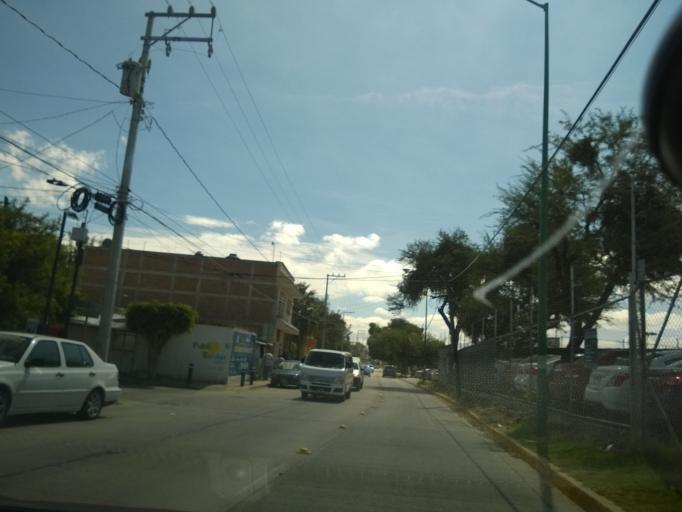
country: MX
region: Guanajuato
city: Leon
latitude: 21.1493
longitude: -101.6833
